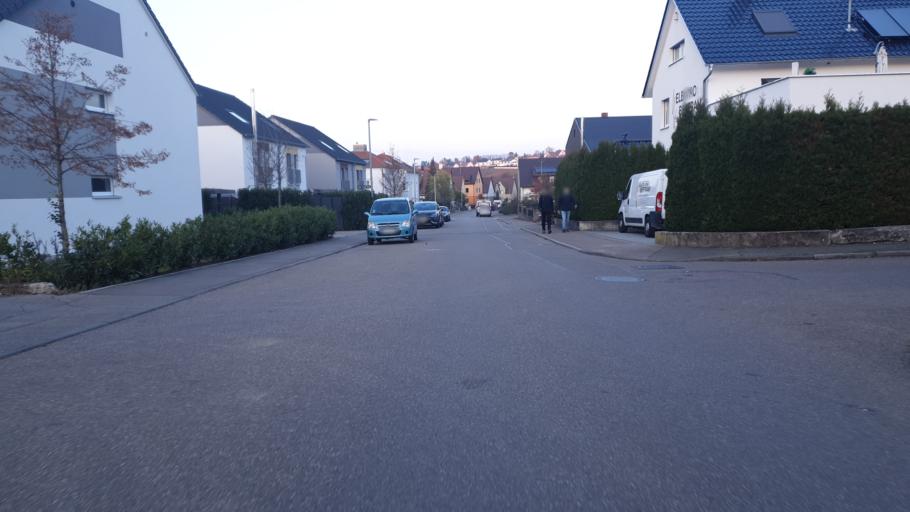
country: DE
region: Baden-Wuerttemberg
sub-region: Regierungsbezirk Stuttgart
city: Flein
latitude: 49.1013
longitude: 9.2075
